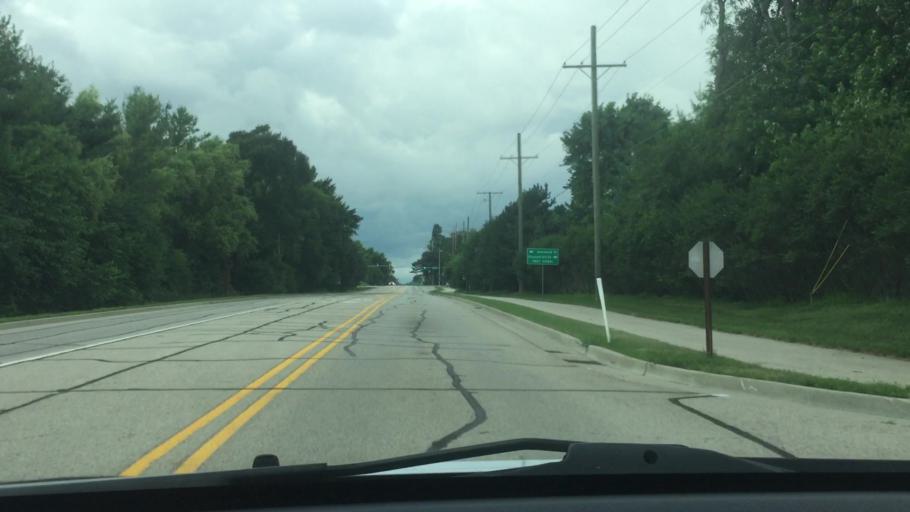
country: US
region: Illinois
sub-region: McHenry County
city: Crystal Lake
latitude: 42.2735
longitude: -88.3208
